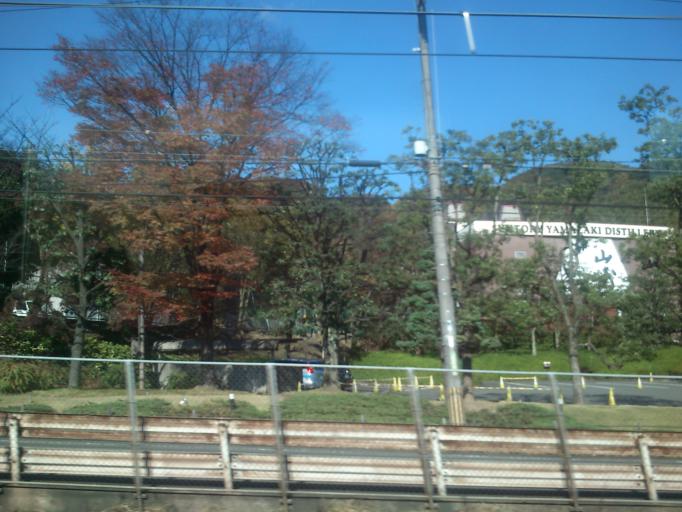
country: JP
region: Kyoto
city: Yawata
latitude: 34.8912
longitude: 135.6741
